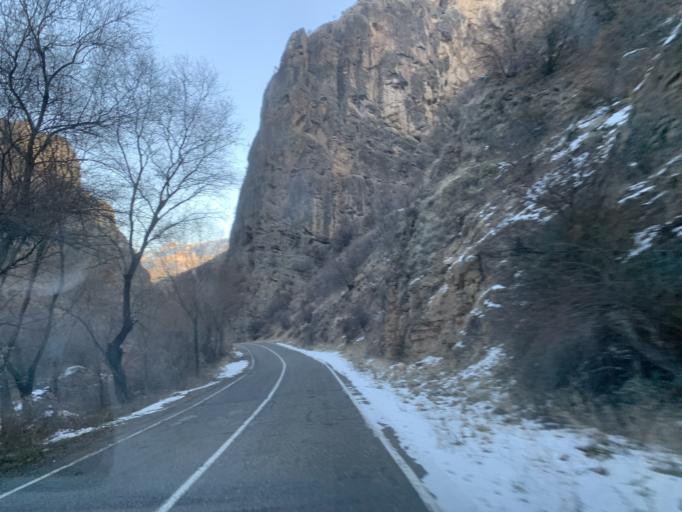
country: AM
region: Vayots' Dzori Marz
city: Areni
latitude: 39.7219
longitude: 45.2050
